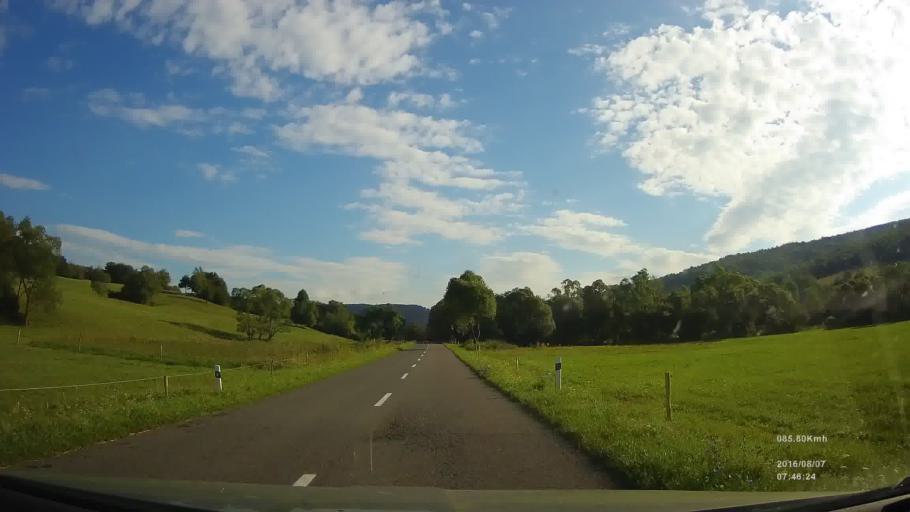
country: SK
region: Presovsky
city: Stropkov
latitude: 49.2692
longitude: 21.7490
